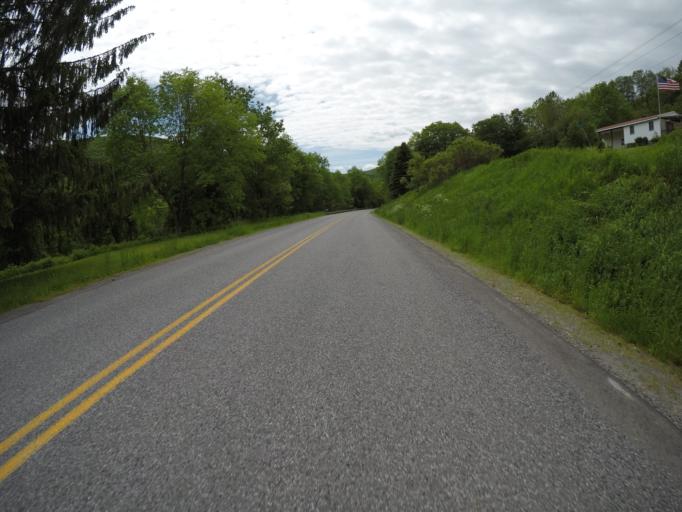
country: US
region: New York
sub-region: Delaware County
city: Stamford
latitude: 42.1932
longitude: -74.5812
